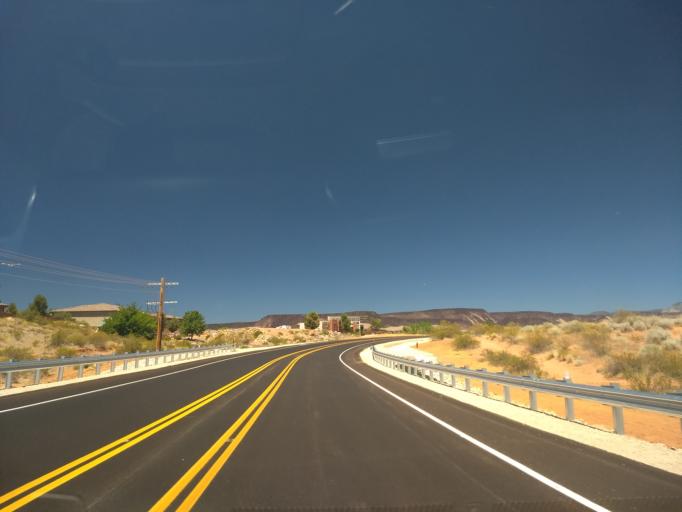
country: US
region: Utah
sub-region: Washington County
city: Washington
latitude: 37.1536
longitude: -113.5186
